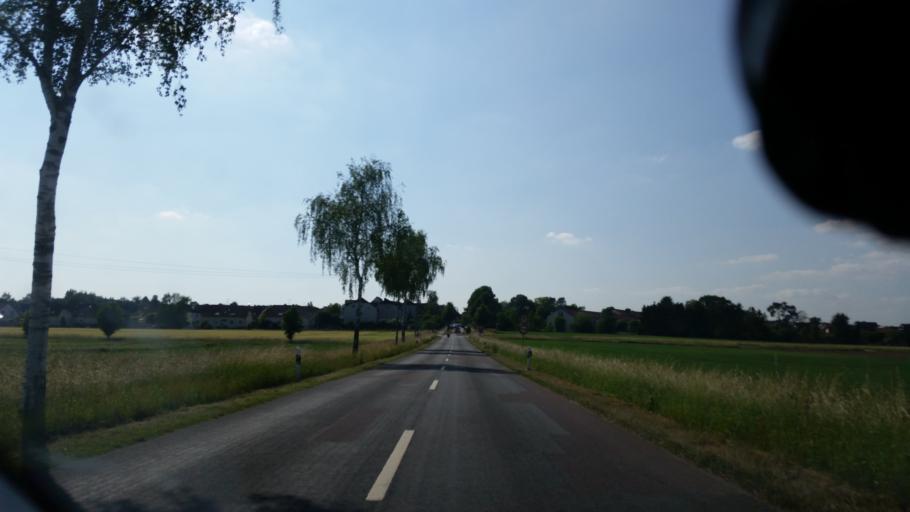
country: DE
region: Lower Saxony
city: Lehre
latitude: 52.3225
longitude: 10.6784
